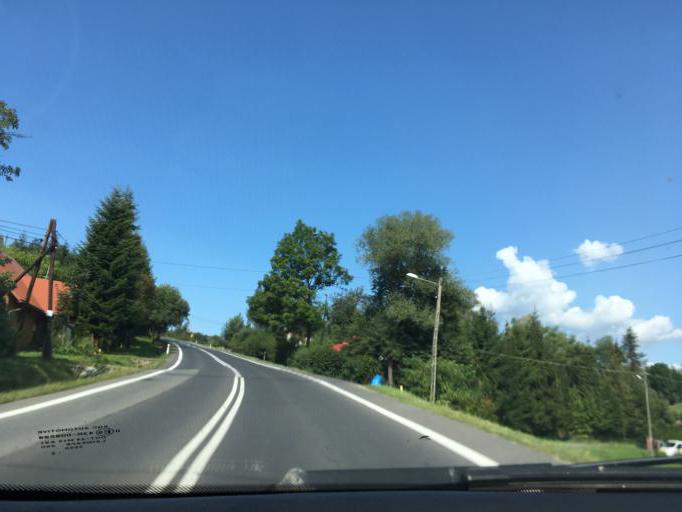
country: PL
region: Subcarpathian Voivodeship
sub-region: Powiat leski
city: Uherce Mineralne
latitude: 49.4656
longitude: 22.3928
